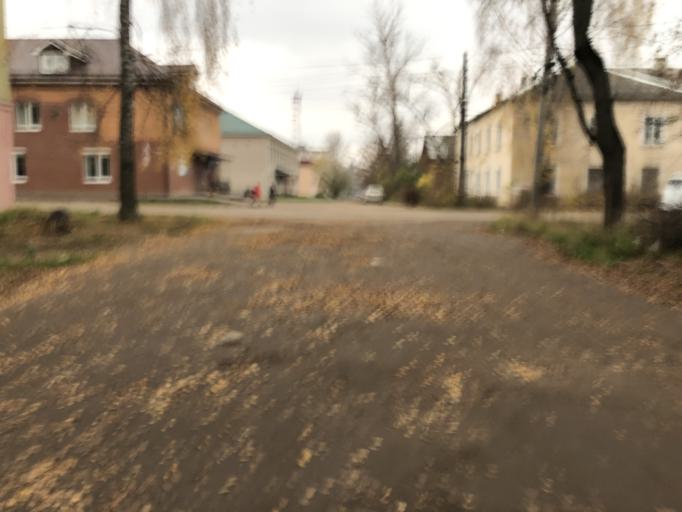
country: RU
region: Tverskaya
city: Rzhev
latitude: 56.2566
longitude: 34.3246
